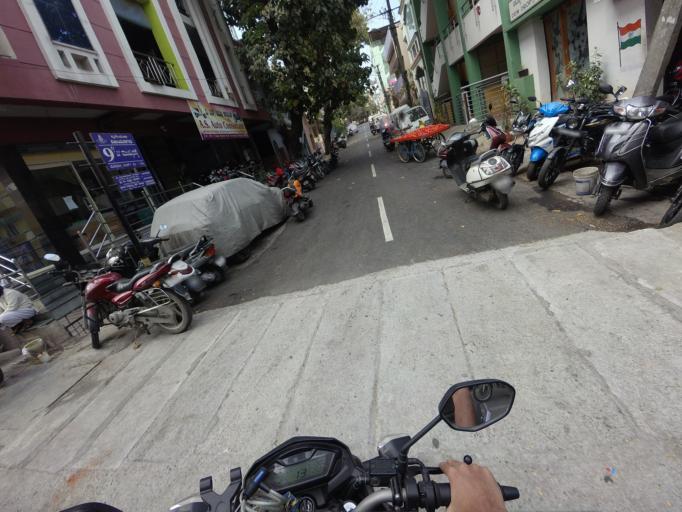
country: IN
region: Karnataka
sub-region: Bangalore Urban
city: Bangalore
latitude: 12.9691
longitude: 77.5457
